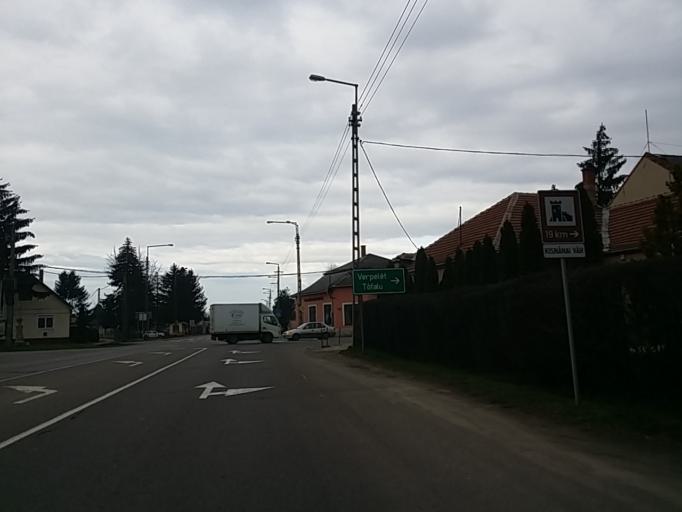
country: HU
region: Heves
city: Kompolt
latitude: 47.7591
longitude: 20.2478
